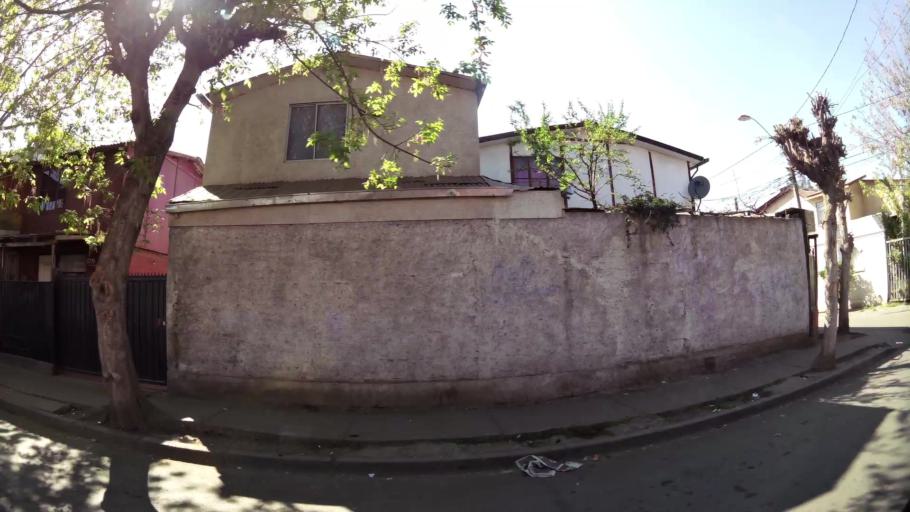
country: CL
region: Santiago Metropolitan
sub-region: Provincia de Chacabuco
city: Chicureo Abajo
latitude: -33.3572
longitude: -70.6893
